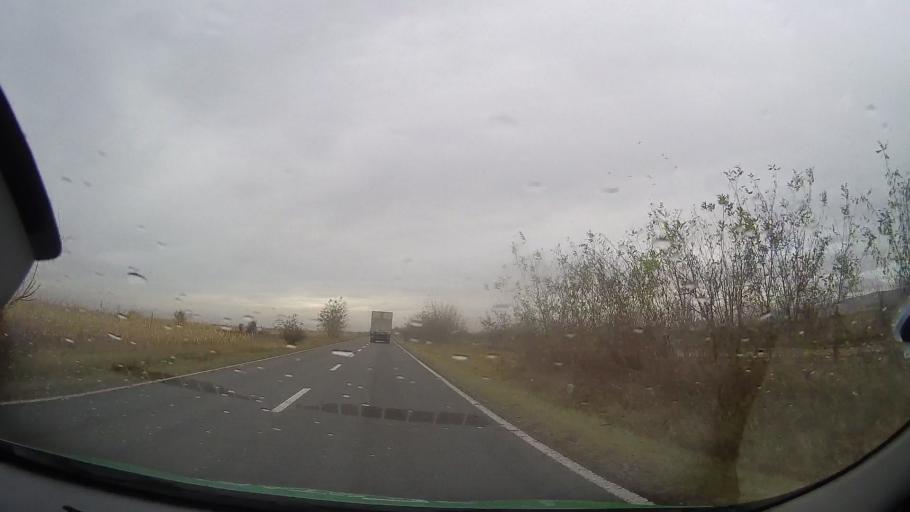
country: RO
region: Prahova
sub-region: Comuna Colceag
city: Inotesti
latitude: 44.9766
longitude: 26.3282
